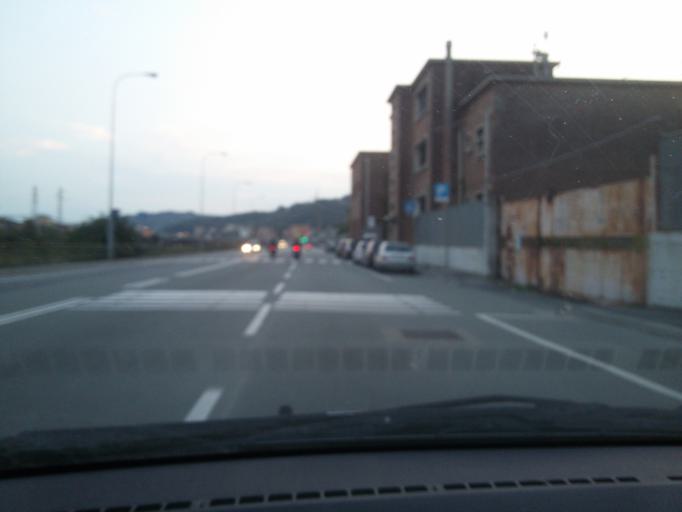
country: IT
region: Liguria
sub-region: Provincia di Genova
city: Genoa
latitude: 44.4555
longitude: 8.8959
